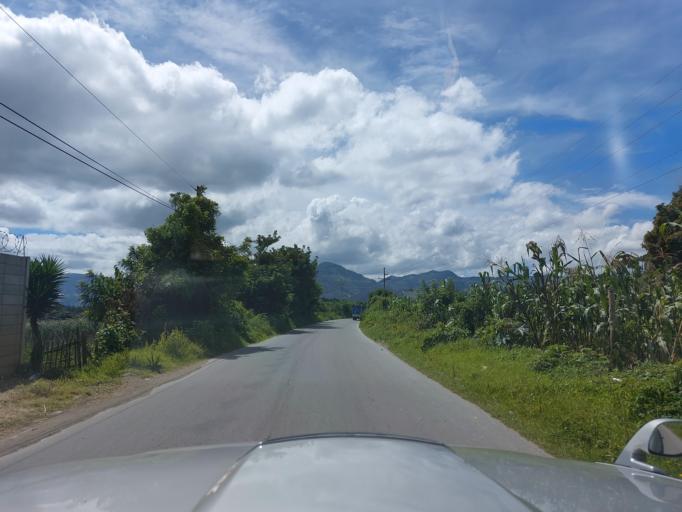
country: GT
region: Chimaltenango
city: San Andres Itzapa
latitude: 14.6158
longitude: -90.8233
